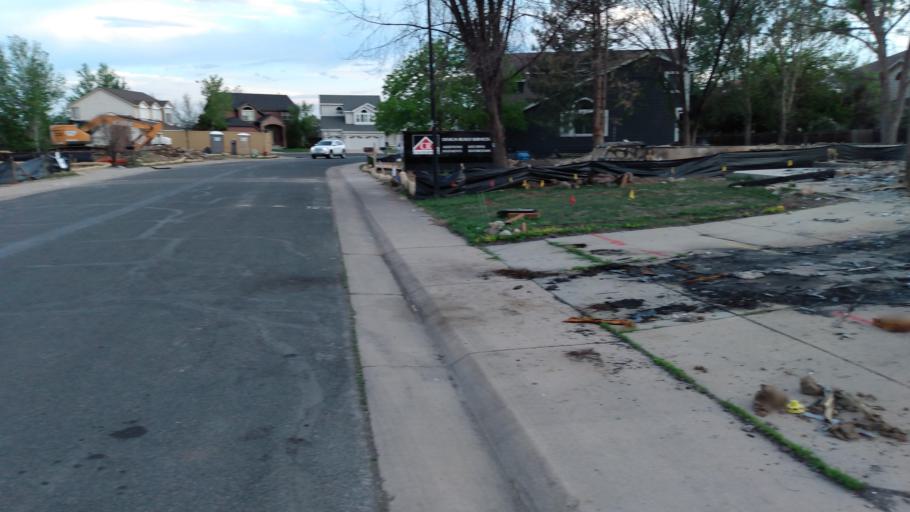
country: US
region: Colorado
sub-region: Boulder County
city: Superior
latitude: 39.9717
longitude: -105.1569
